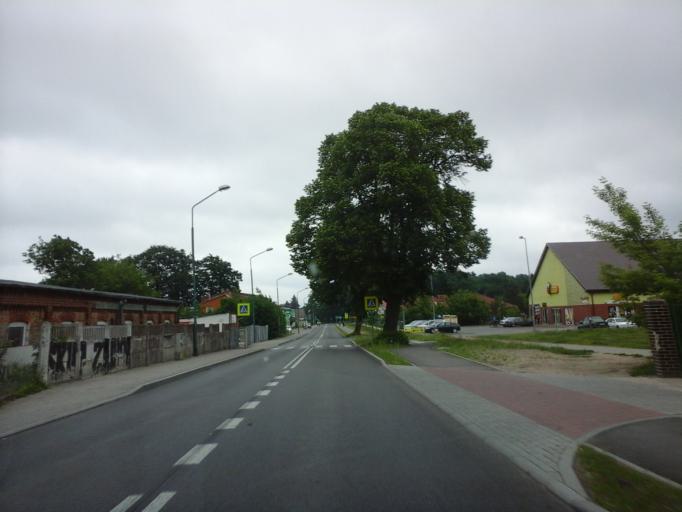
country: PL
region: West Pomeranian Voivodeship
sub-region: Powiat drawski
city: Kalisz Pomorski
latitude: 53.2905
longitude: 15.8987
